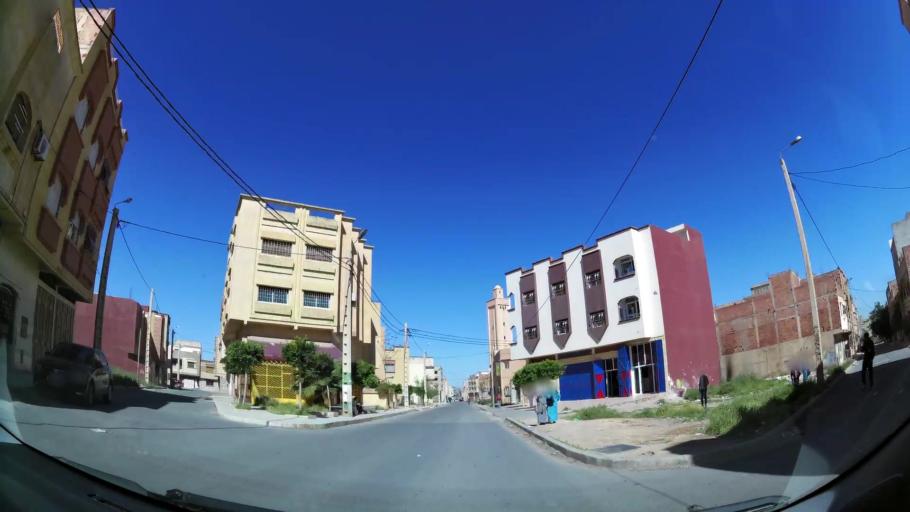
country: MA
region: Oriental
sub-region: Oujda-Angad
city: Oujda
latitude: 34.6597
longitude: -1.8841
